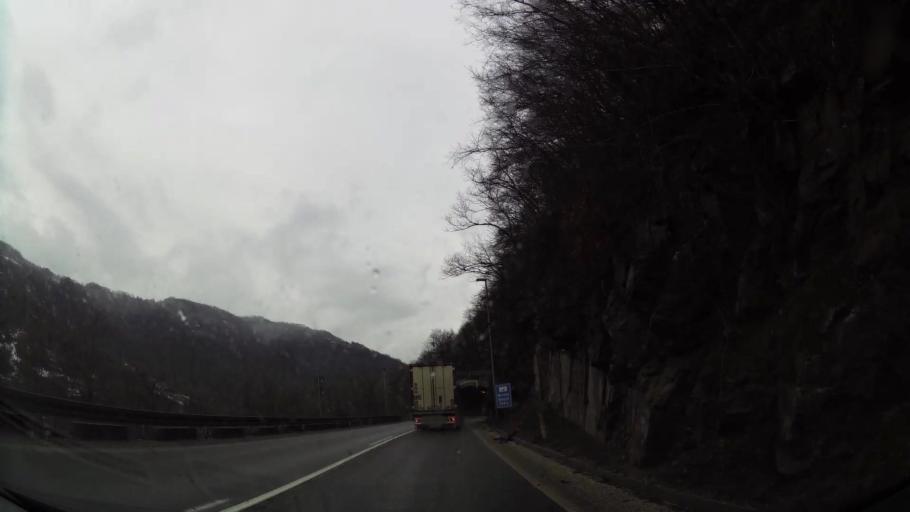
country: RS
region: Central Serbia
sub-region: Pcinjski Okrug
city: Vladicin Han
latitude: 42.7485
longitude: 22.0637
